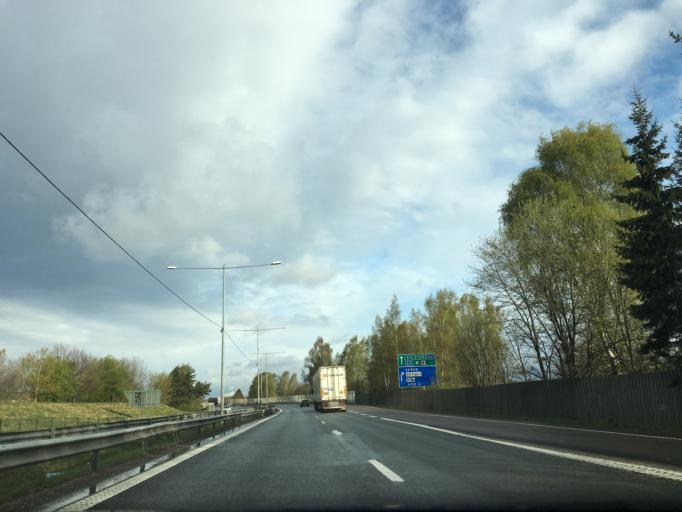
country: SE
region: Vaermland
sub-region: Karlstads Kommun
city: Karlstad
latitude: 59.3965
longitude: 13.5125
